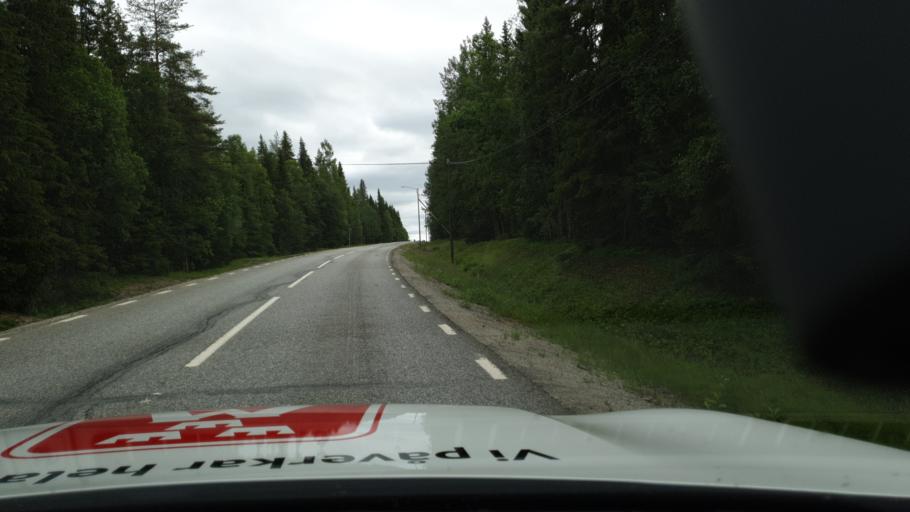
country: SE
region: Vaesterbotten
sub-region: Lycksele Kommun
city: Soderfors
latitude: 64.6534
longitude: 17.8472
